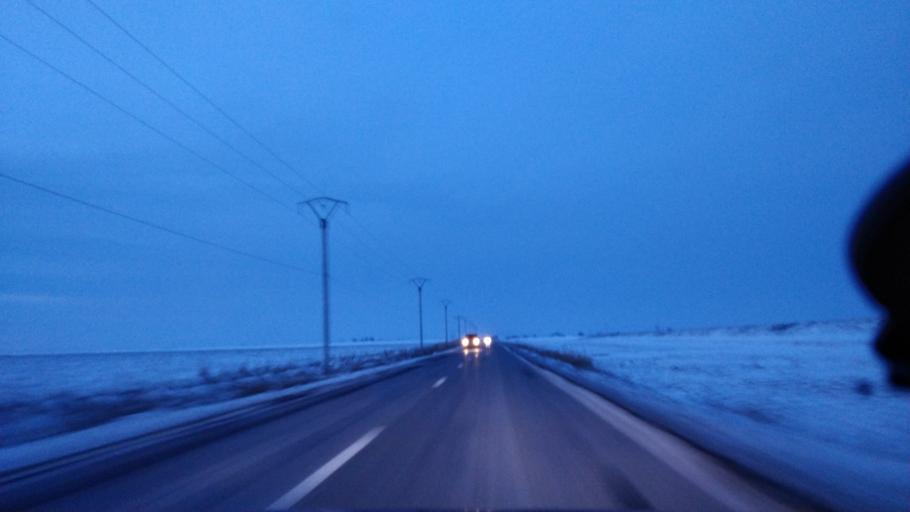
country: RO
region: Vrancea
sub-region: Comuna Nanesti
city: Nanesti
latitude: 45.5681
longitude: 27.4989
